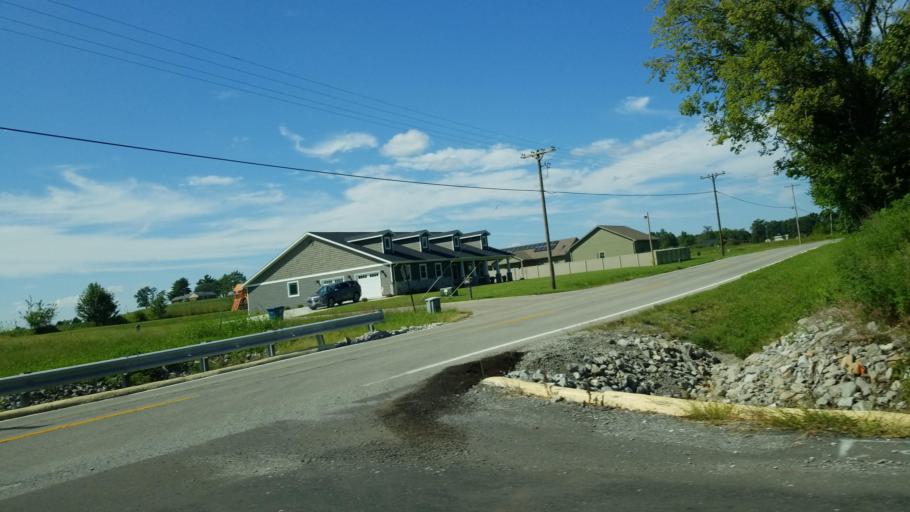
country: US
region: Illinois
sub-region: Williamson County
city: Marion
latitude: 37.7445
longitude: -88.8924
